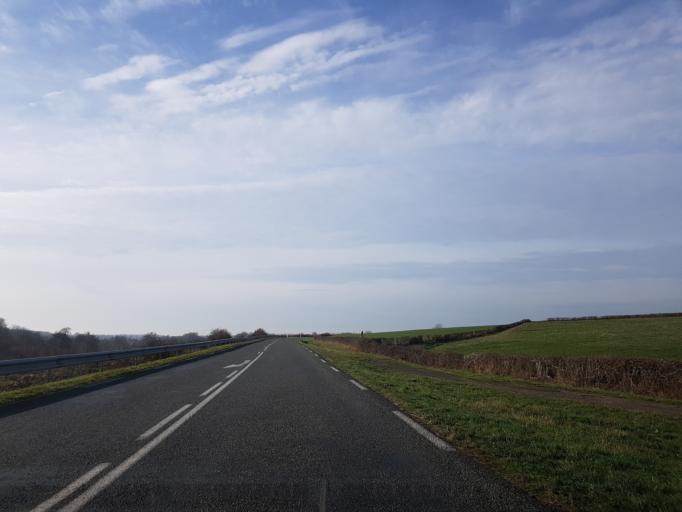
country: FR
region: Bourgogne
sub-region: Departement de Saone-et-Loire
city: Bourbon-Lancy
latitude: 46.6071
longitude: 3.8217
